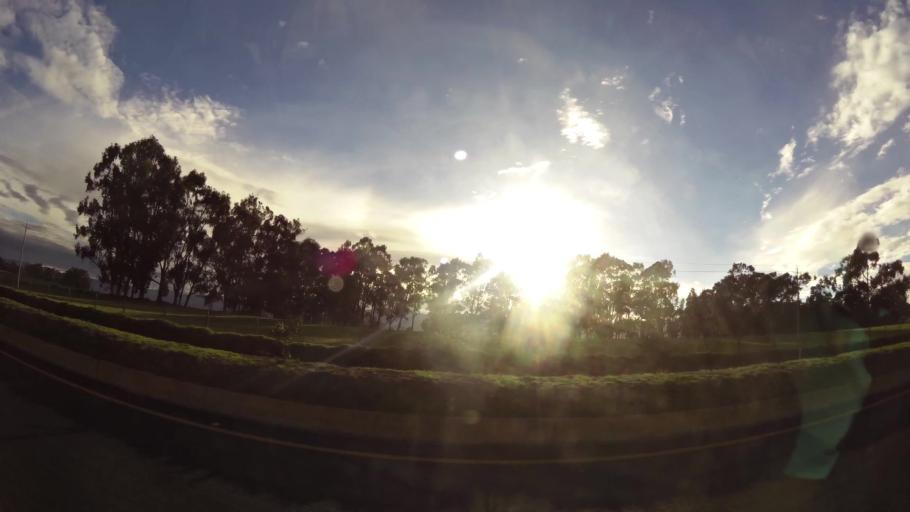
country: EC
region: Cotopaxi
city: Saquisili
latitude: -0.8221
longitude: -78.6228
